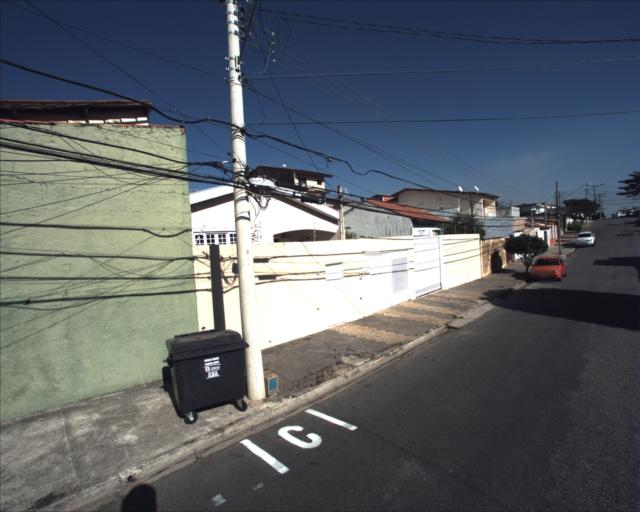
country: BR
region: Sao Paulo
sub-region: Sorocaba
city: Sorocaba
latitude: -23.5048
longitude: -47.4231
